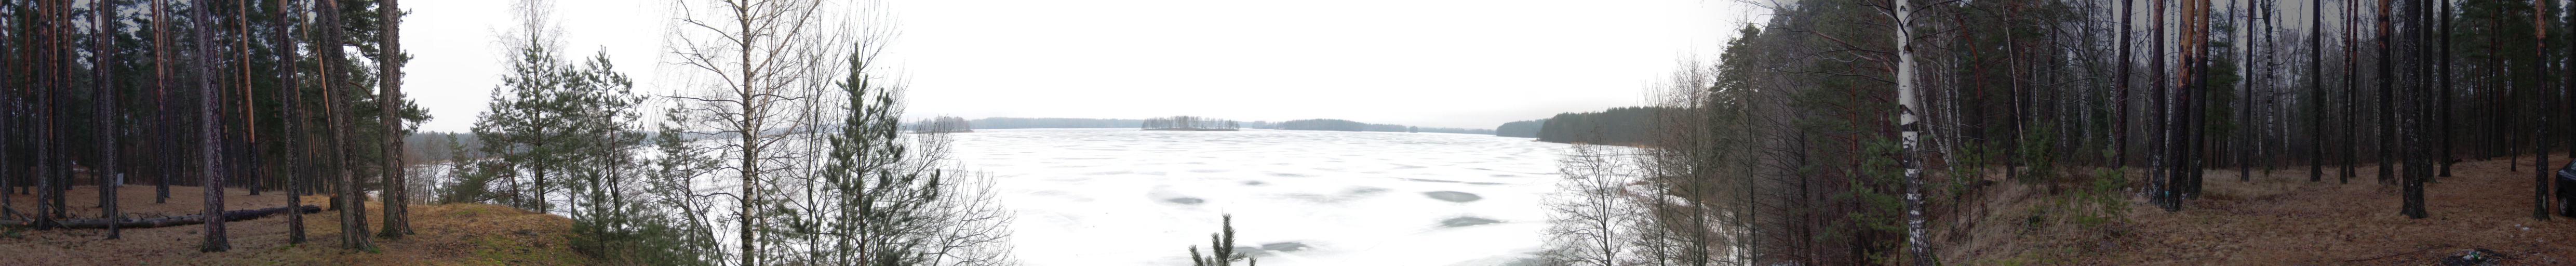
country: LT
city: Zarasai
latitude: 55.6340
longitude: 26.0691
